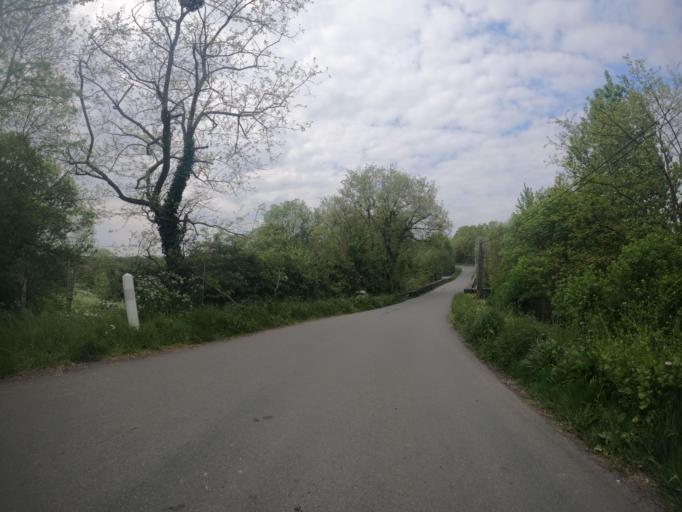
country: FR
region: Poitou-Charentes
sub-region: Departement des Deux-Sevres
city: Saint-Varent
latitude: 46.8587
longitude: -0.2594
